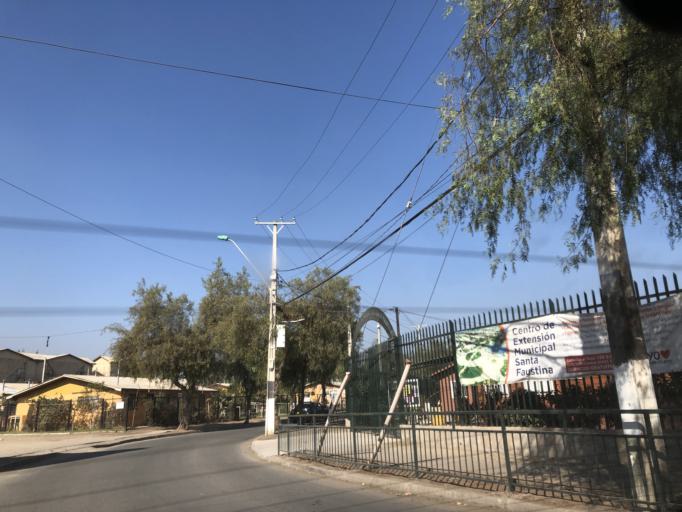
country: CL
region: Santiago Metropolitan
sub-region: Provincia de Cordillera
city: Puente Alto
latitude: -33.6271
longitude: -70.5950
